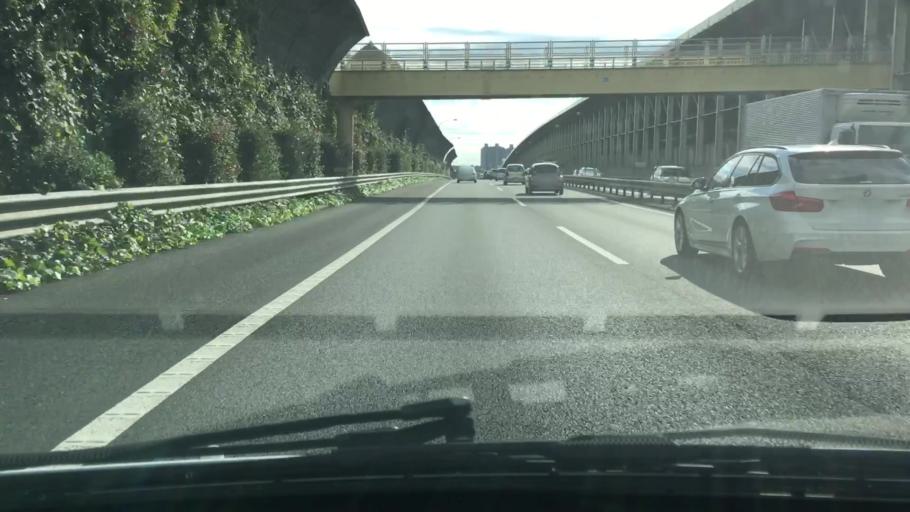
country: JP
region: Chiba
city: Chiba
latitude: 35.6379
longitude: 140.1189
